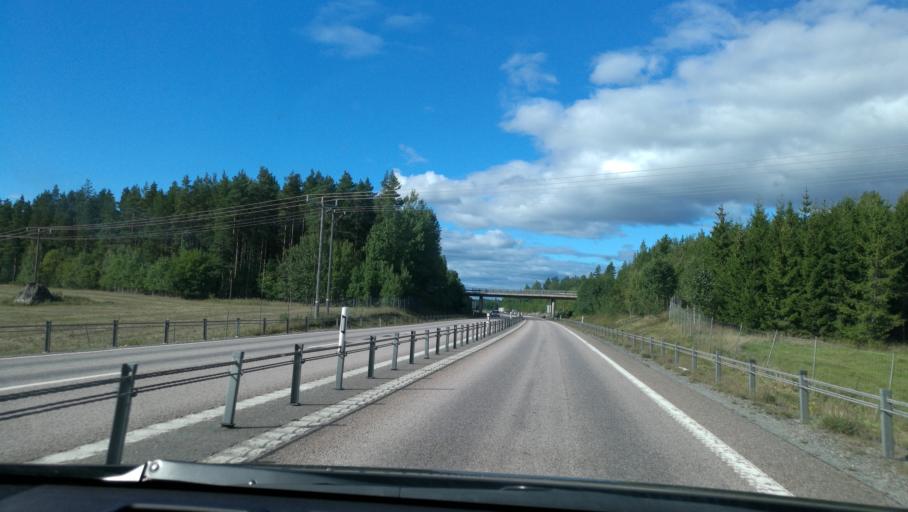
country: SE
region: Soedermanland
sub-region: Eskilstuna Kommun
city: Kvicksund
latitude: 59.4314
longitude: 16.3618
